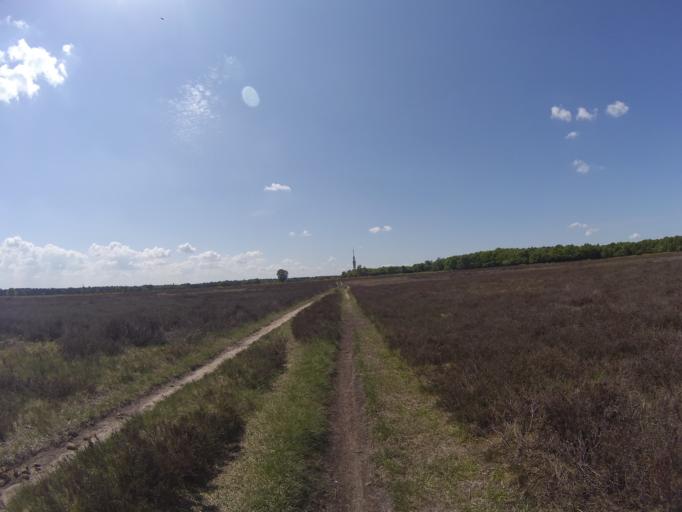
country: NL
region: North Holland
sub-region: Gemeente Hilversum
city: Hilversum
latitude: 52.2518
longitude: 5.1890
